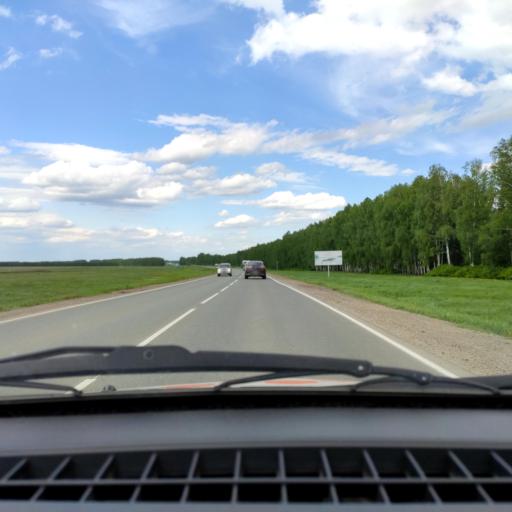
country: RU
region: Bashkortostan
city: Iglino
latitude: 54.9711
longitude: 56.4995
